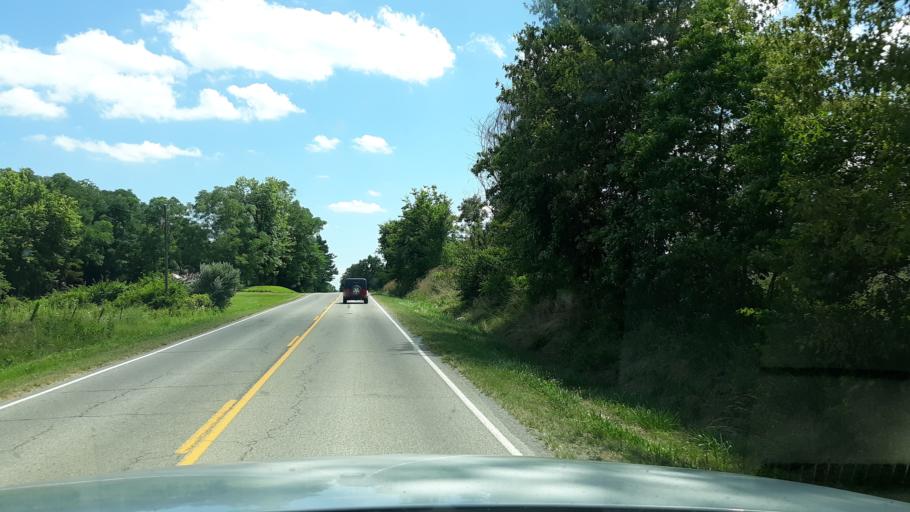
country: US
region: Illinois
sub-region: Saline County
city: Harrisburg
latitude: 37.8540
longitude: -88.6056
